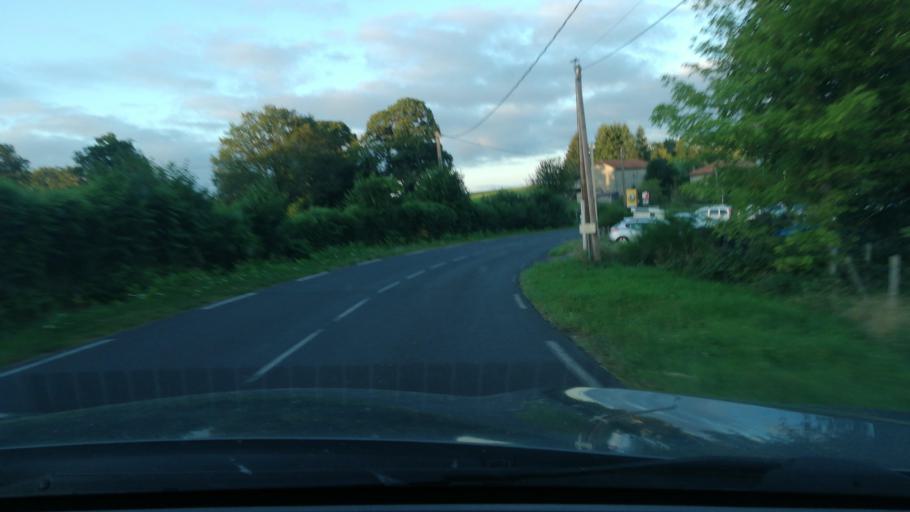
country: FR
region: Auvergne
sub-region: Departement du Cantal
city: Laroquebrou
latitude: 44.9599
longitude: 2.1351
